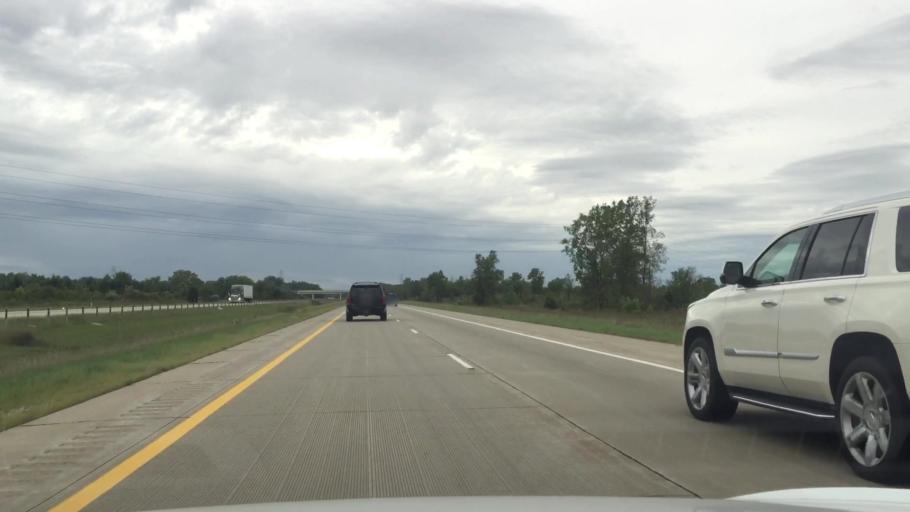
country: US
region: Michigan
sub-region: Macomb County
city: Richmond
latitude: 42.7572
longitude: -82.7033
